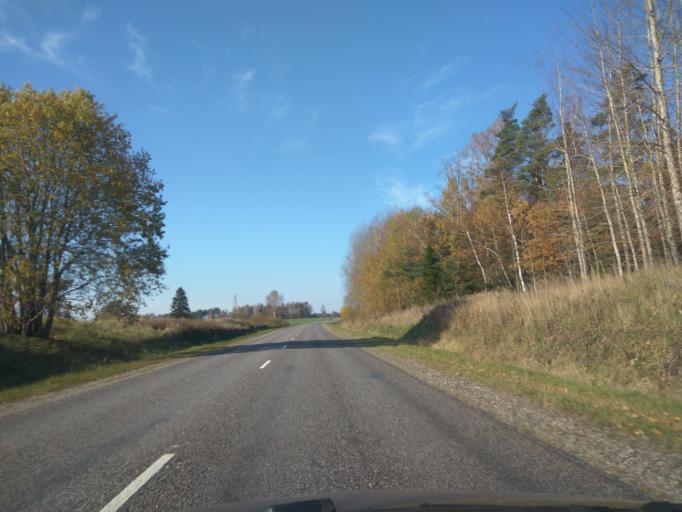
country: LV
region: Kuldigas Rajons
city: Kuldiga
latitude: 57.0302
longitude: 21.8488
